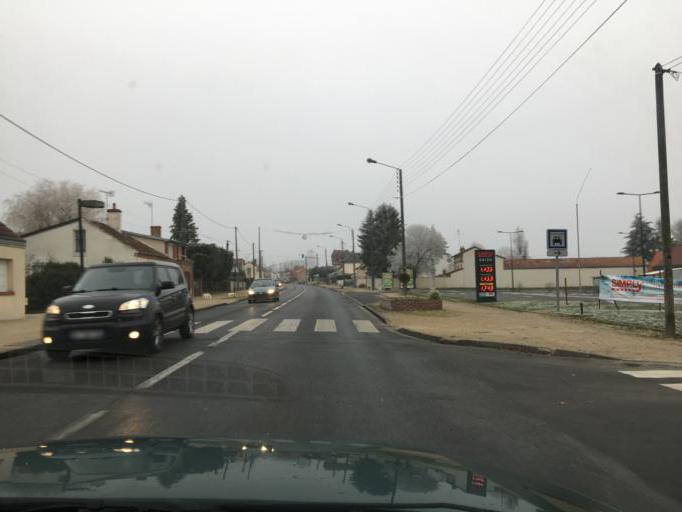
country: FR
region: Centre
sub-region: Departement du Loiret
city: La Ferte-Saint-Aubin
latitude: 47.7173
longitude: 1.9413
